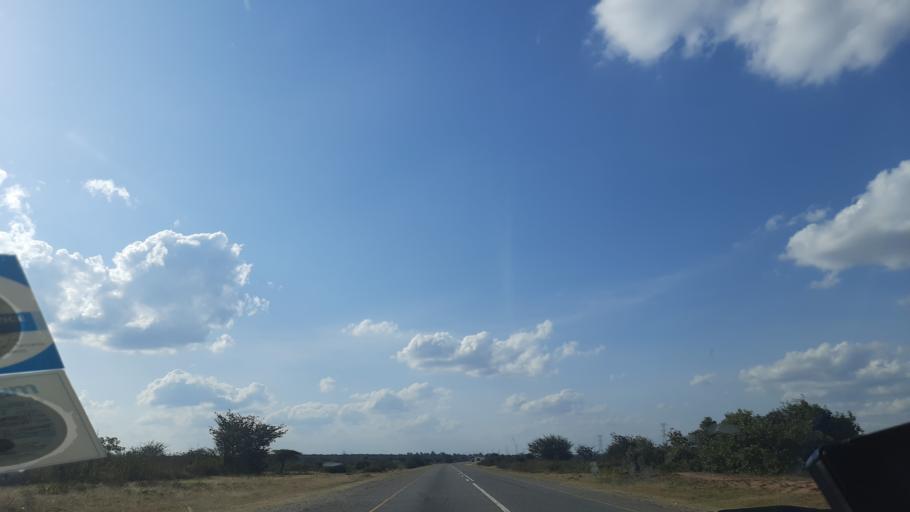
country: TZ
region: Singida
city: Ikungi
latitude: -5.1906
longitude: 34.7833
